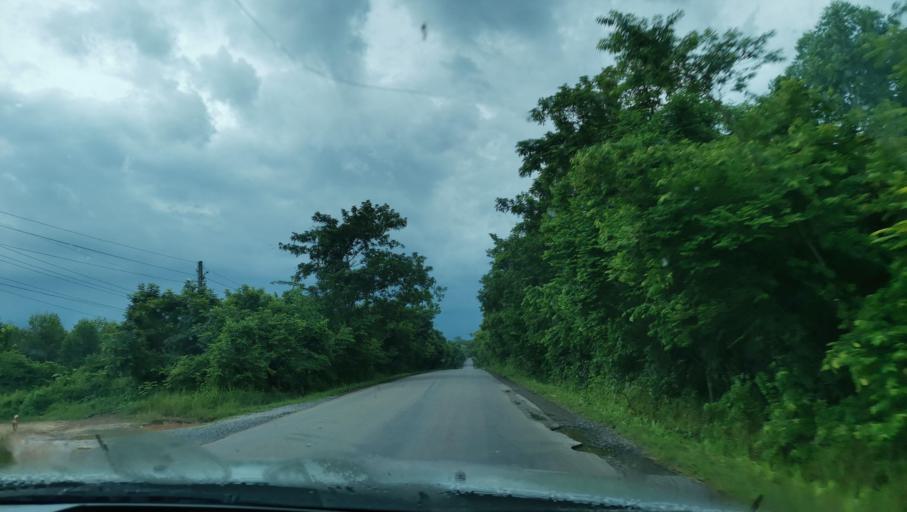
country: TH
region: Nakhon Phanom
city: Ban Phaeng
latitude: 17.8643
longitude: 104.4222
